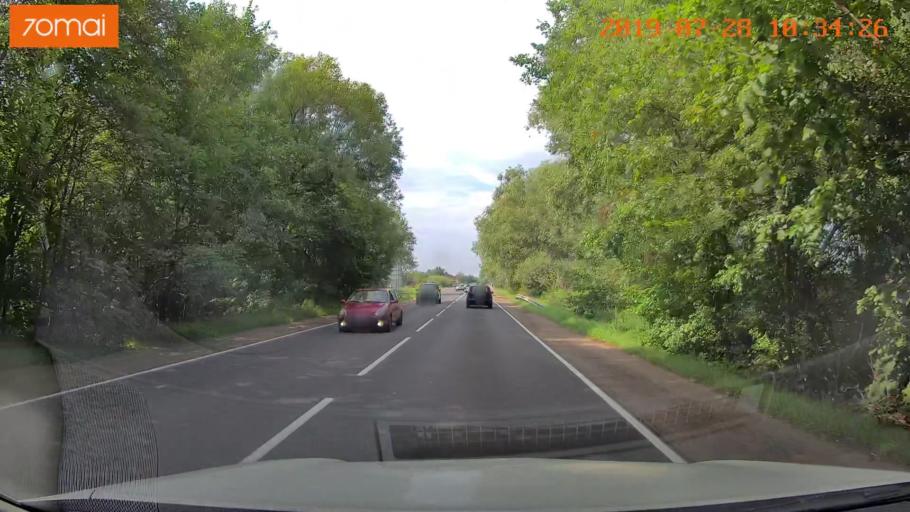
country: RU
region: Kaliningrad
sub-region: Gorod Kaliningrad
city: Kaliningrad
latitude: 54.7535
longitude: 20.4393
